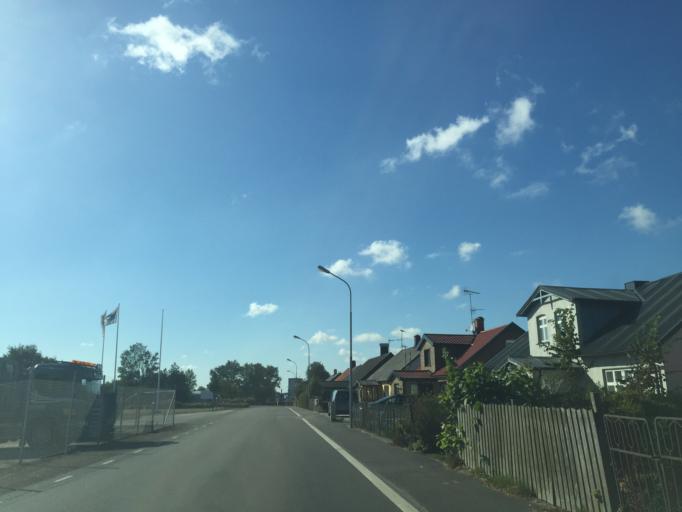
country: SE
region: Skane
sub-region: Ystads Kommun
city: Kopingebro
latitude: 55.4496
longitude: 14.0229
